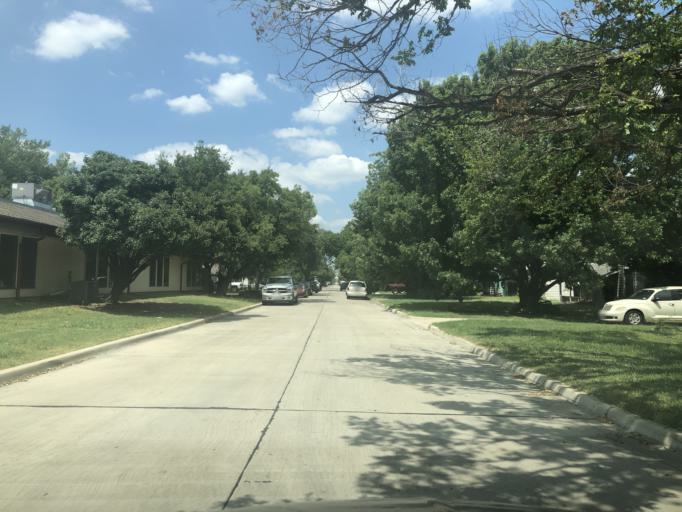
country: US
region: Texas
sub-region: Dallas County
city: Grand Prairie
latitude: 32.7478
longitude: -97.0104
